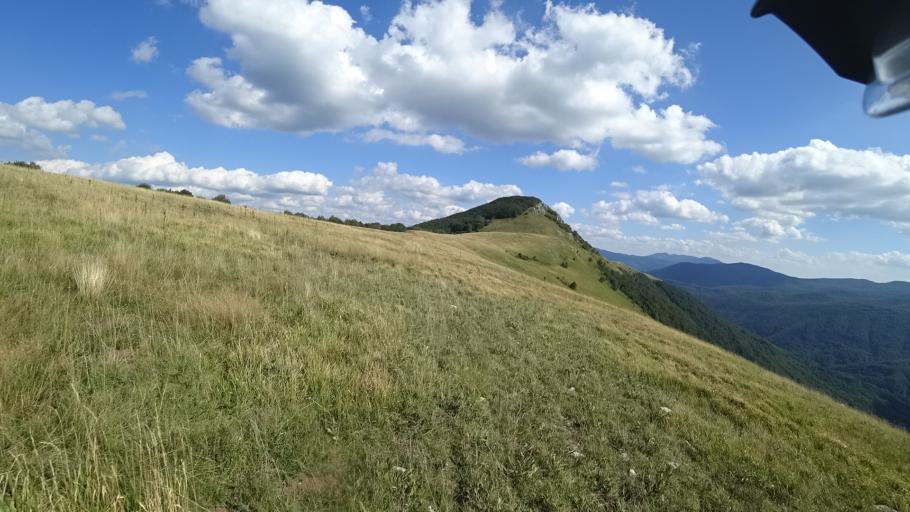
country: HR
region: Zadarska
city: Gracac
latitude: 44.3869
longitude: 16.0408
